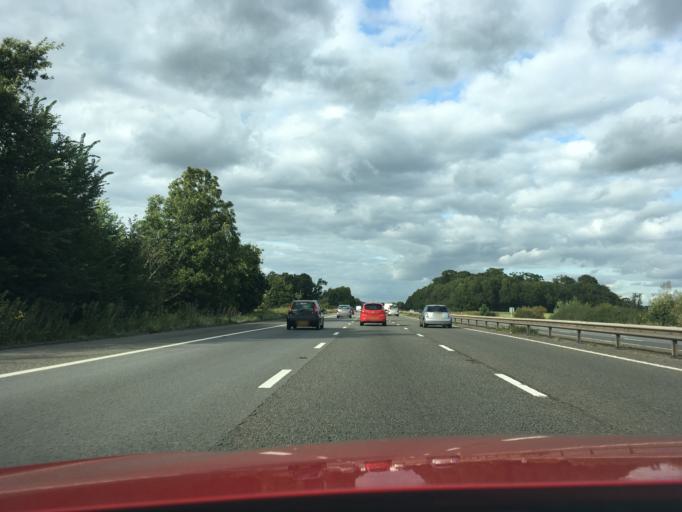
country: GB
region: England
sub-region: Gloucestershire
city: Dursley
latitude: 51.7320
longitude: -2.3466
